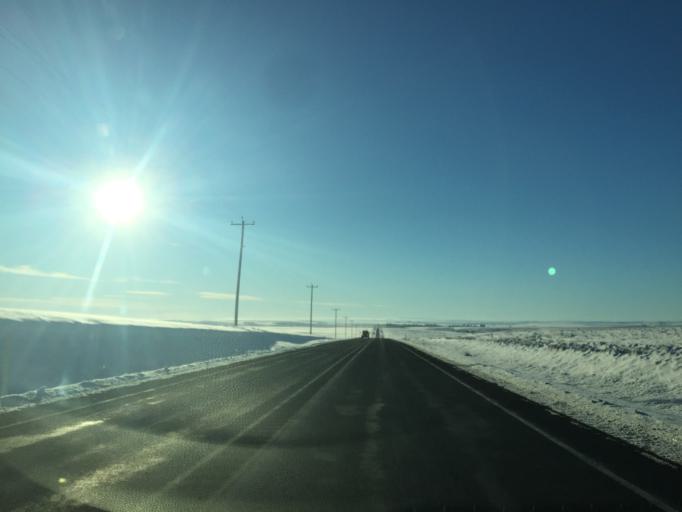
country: US
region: Washington
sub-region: Okanogan County
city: Coulee Dam
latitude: 47.7324
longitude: -118.8631
